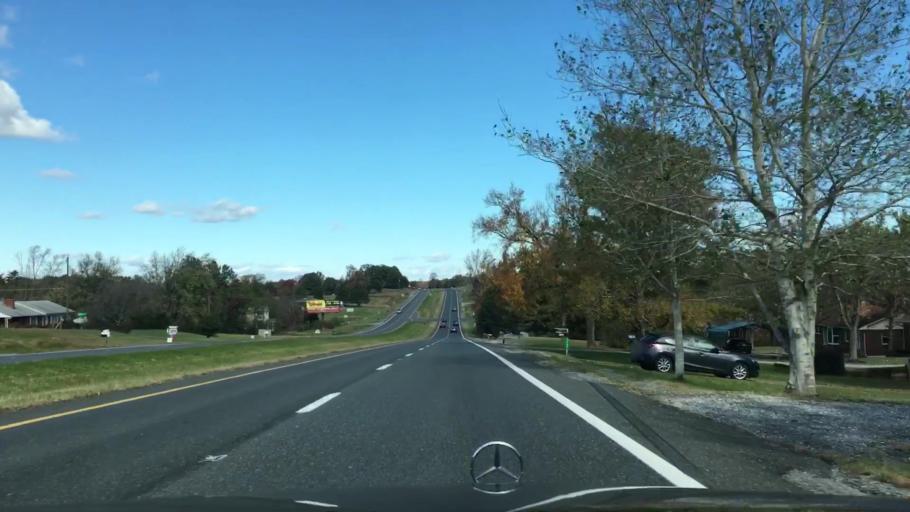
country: US
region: Virginia
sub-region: Campbell County
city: Altavista
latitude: 37.1789
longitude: -79.2052
